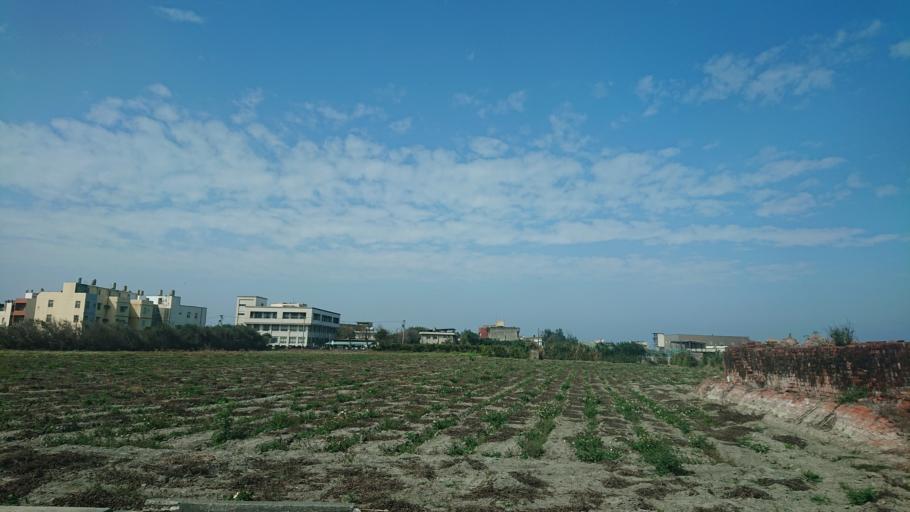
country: TW
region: Taiwan
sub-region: Changhua
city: Chang-hua
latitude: 23.9247
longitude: 120.3227
